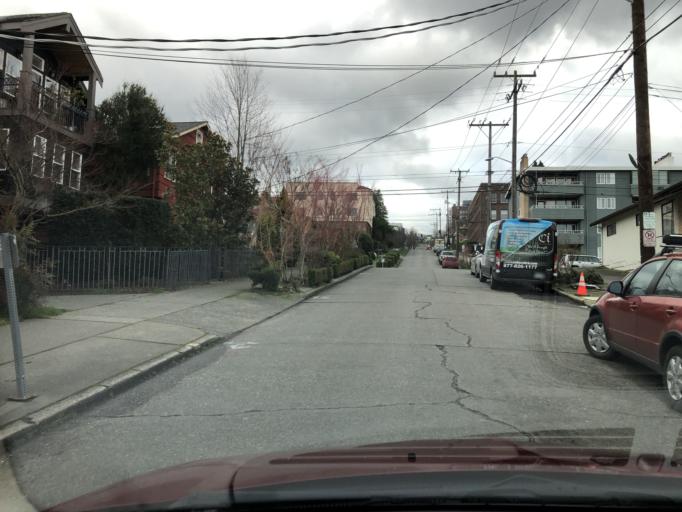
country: US
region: Washington
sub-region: King County
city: Seattle
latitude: 47.6396
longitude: -122.3290
